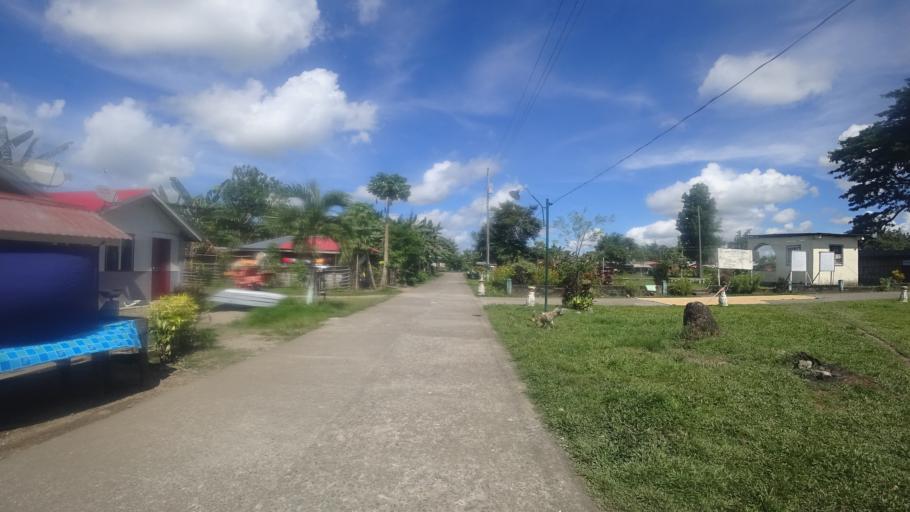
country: PH
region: Eastern Visayas
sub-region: Province of Leyte
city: Pastrana
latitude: 11.1546
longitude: 124.8599
